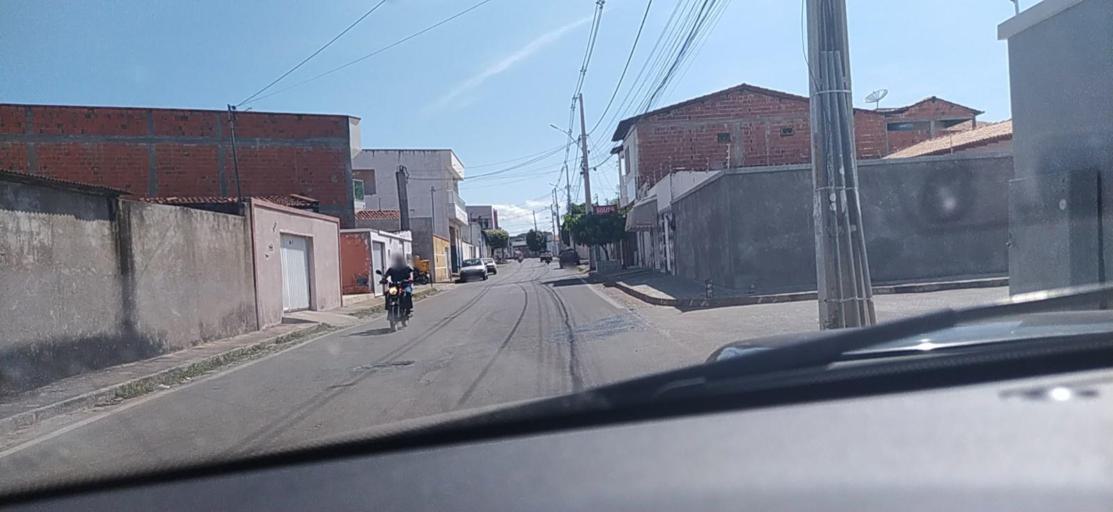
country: BR
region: Bahia
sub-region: Guanambi
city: Guanambi
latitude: -14.2156
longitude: -42.7684
